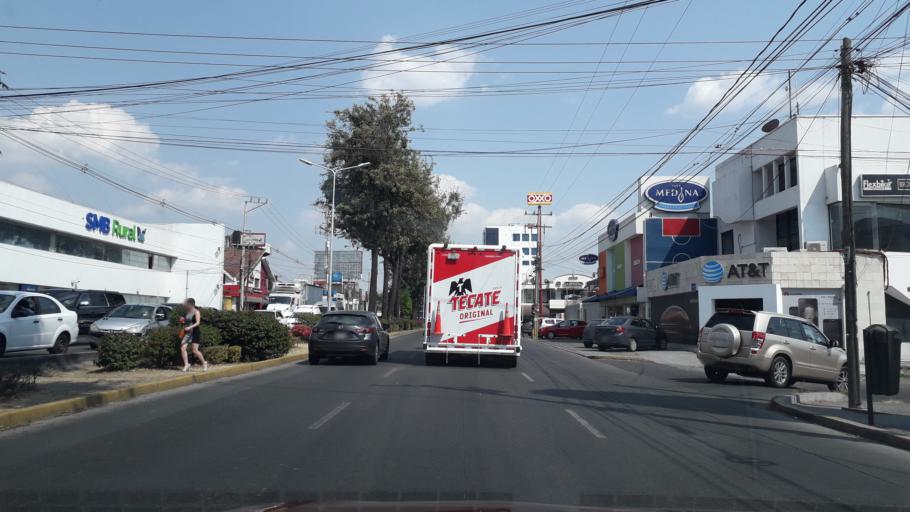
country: MX
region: Puebla
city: Puebla
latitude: 19.0412
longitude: -98.2295
